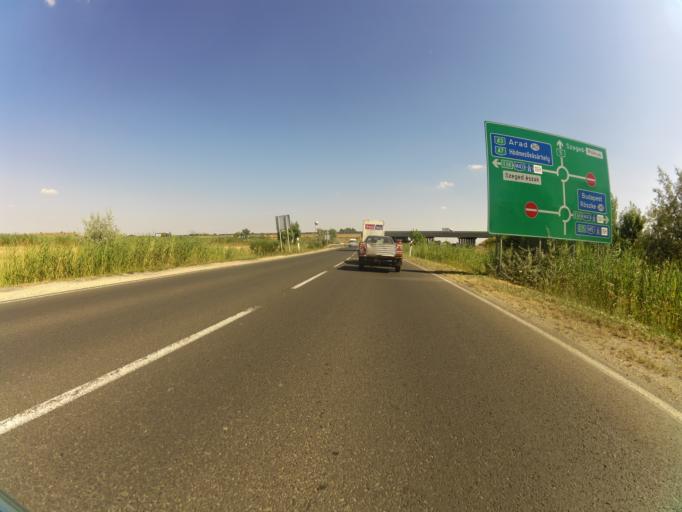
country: HU
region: Csongrad
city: Szatymaz
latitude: 46.2949
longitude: 20.0810
